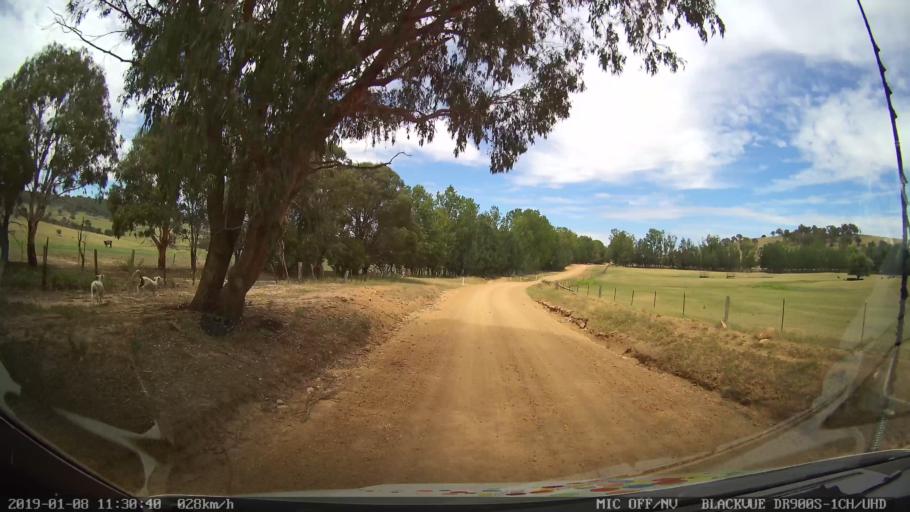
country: AU
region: New South Wales
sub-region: Guyra
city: Guyra
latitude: -30.3091
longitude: 151.5429
